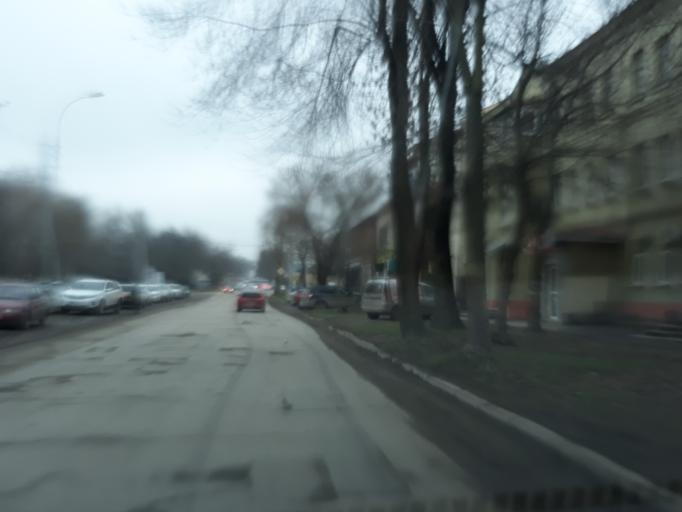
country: RU
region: Rostov
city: Taganrog
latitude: 47.2225
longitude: 38.9229
